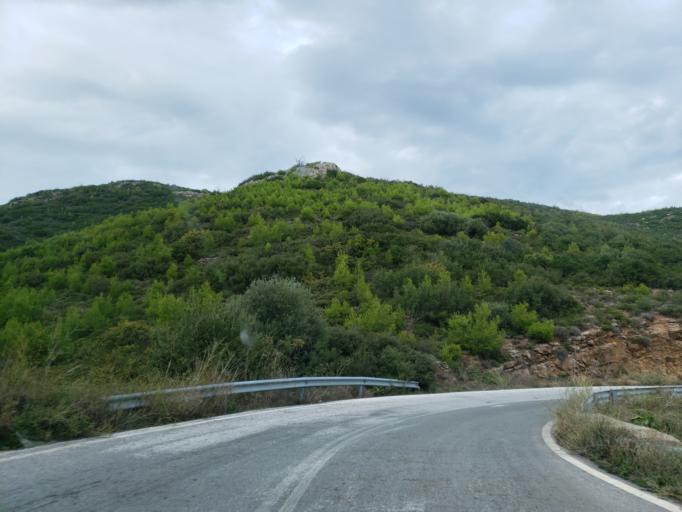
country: GR
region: Attica
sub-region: Nomarchia Anatolikis Attikis
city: Grammatiko
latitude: 38.2111
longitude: 23.9465
